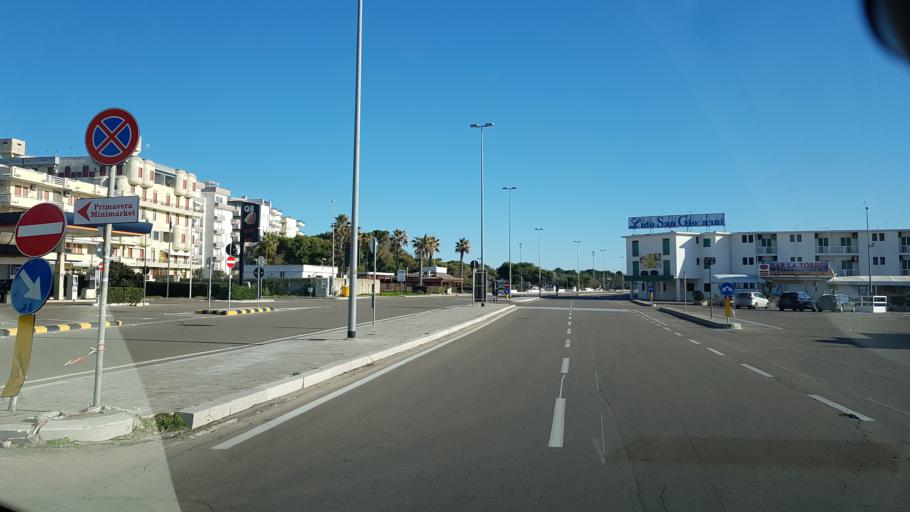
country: IT
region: Apulia
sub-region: Provincia di Lecce
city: Gallipoli
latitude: 40.0486
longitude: 18.0023
